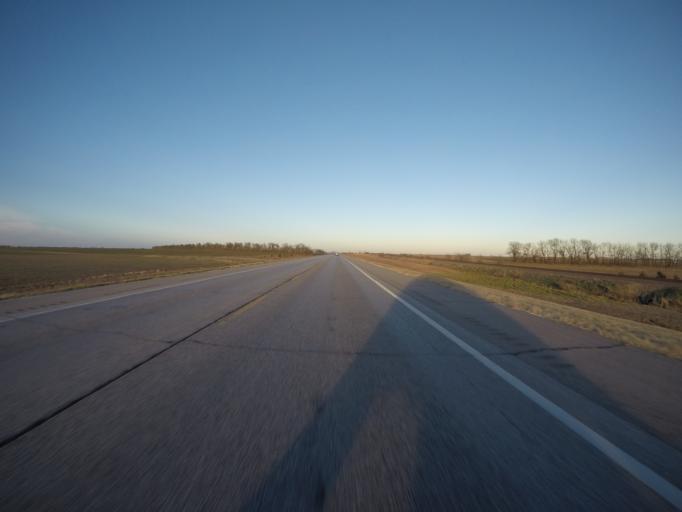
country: US
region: Kansas
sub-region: Harvey County
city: North Newton
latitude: 38.1330
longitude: -97.2387
